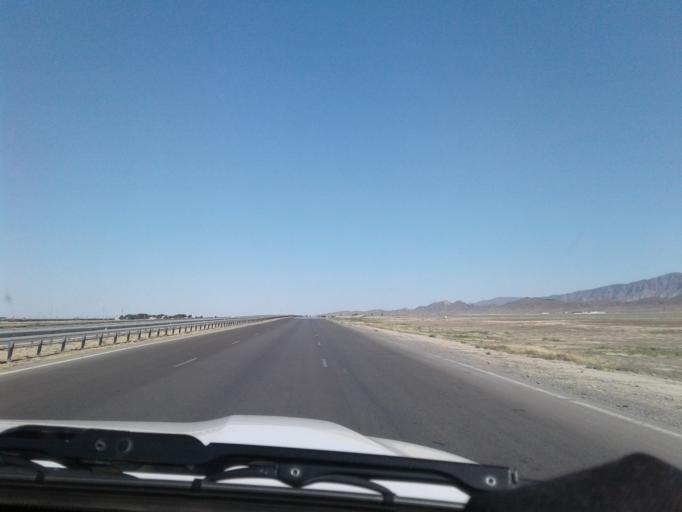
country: IR
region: Razavi Khorasan
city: Dargaz
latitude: 37.7314
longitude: 58.9924
